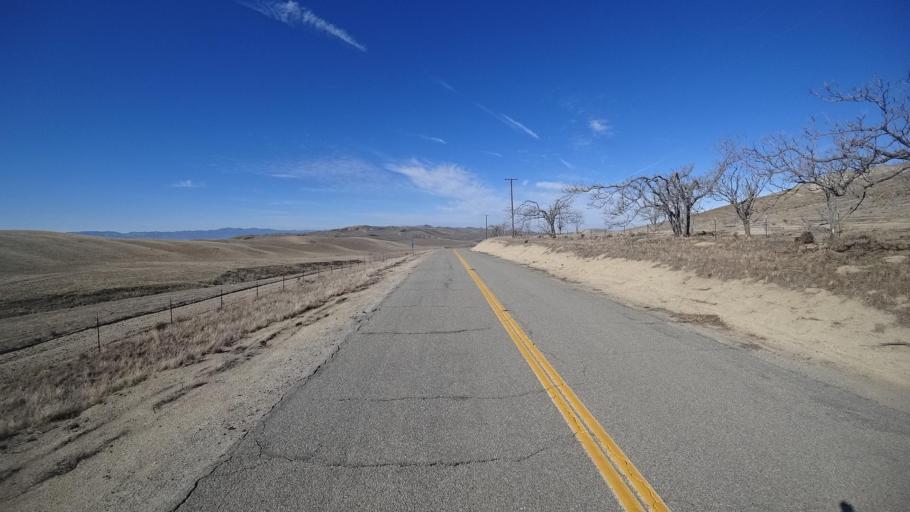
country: US
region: California
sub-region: Kern County
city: Maricopa
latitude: 34.9538
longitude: -119.4313
